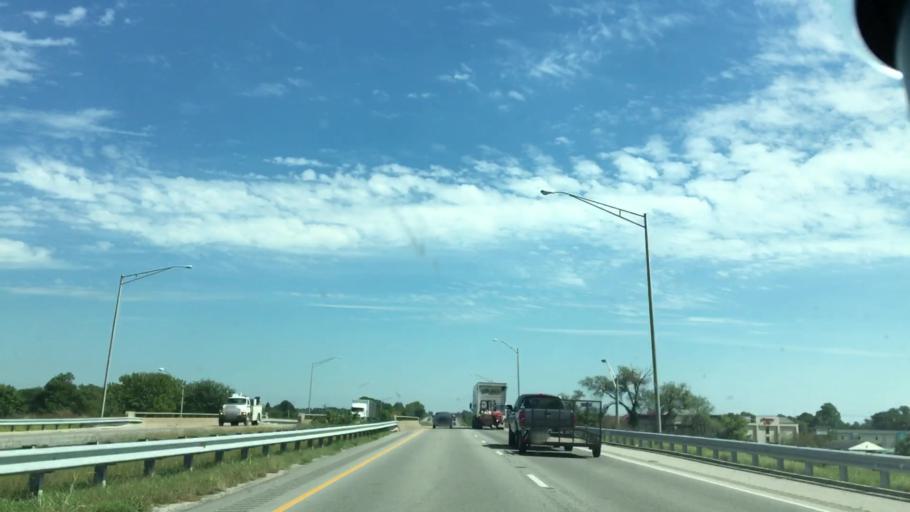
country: US
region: Kentucky
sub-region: Daviess County
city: Owensboro
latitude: 37.7287
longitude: -87.1235
